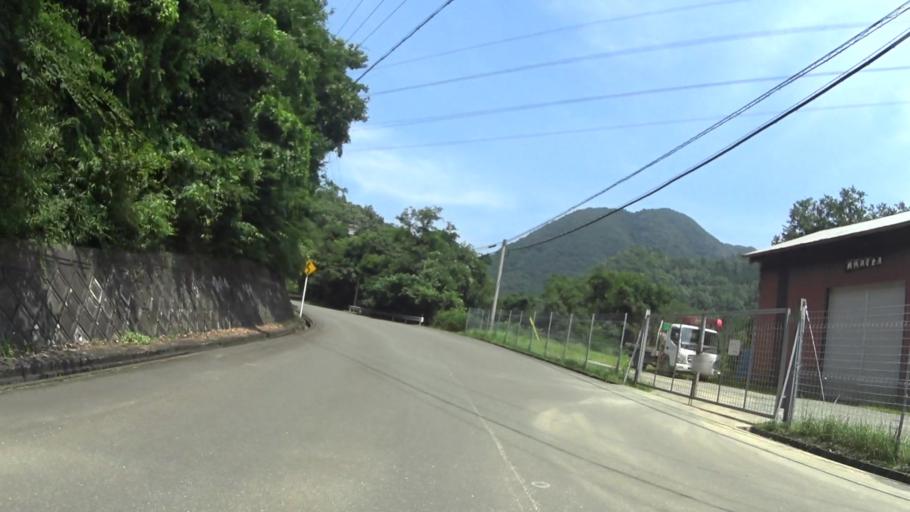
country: JP
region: Kyoto
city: Ayabe
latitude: 35.2777
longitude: 135.4314
